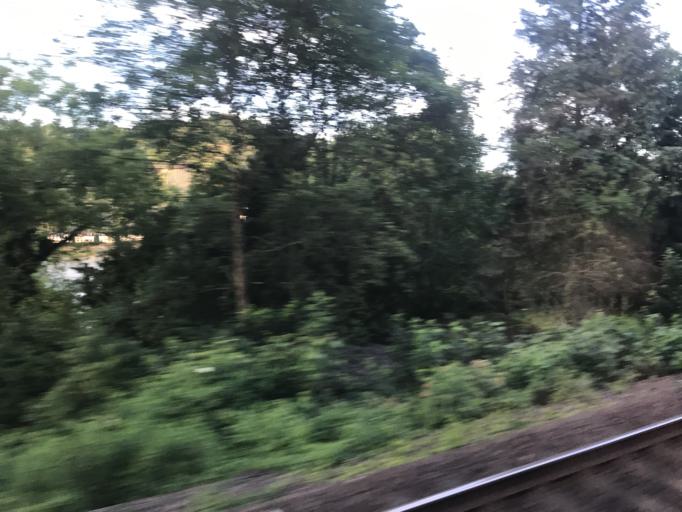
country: DE
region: Rheinland-Pfalz
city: Oberdiebach
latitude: 50.0467
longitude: 7.7812
